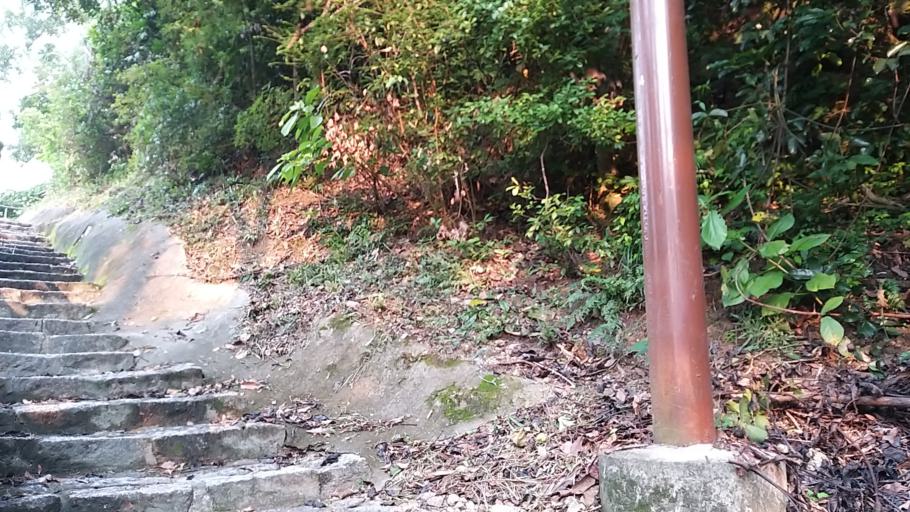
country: HK
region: Tuen Mun
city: Tuen Mun
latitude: 22.4037
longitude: 113.9824
